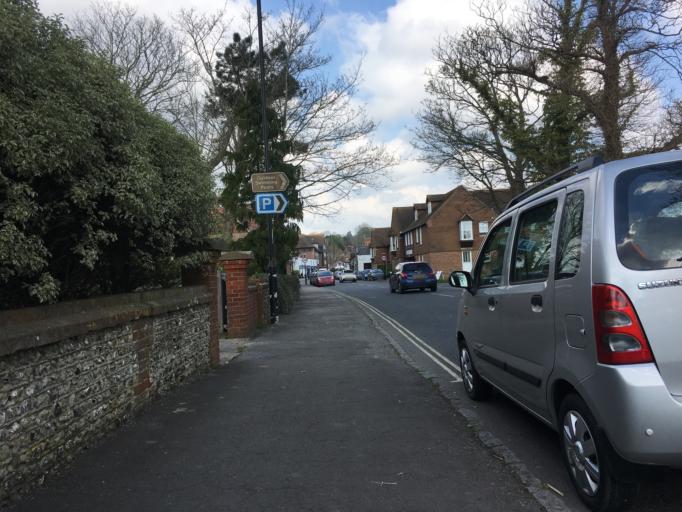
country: GB
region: England
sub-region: West Sussex
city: Arundel
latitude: 50.8519
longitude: -0.5508
